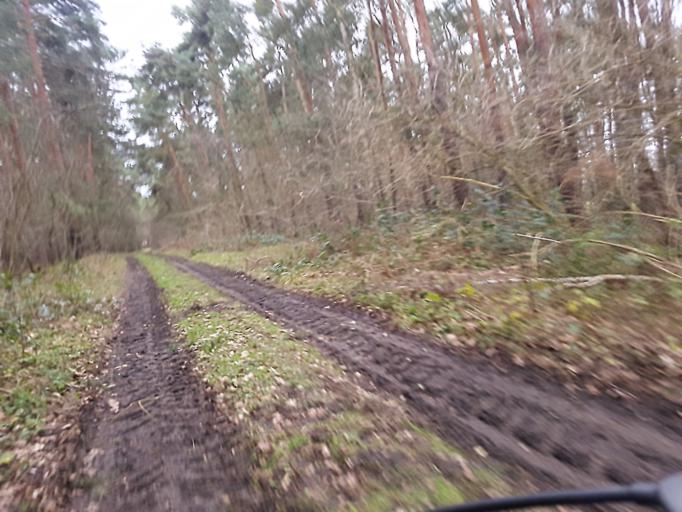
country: DE
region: Brandenburg
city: Schilda
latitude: 51.5776
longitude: 13.3985
